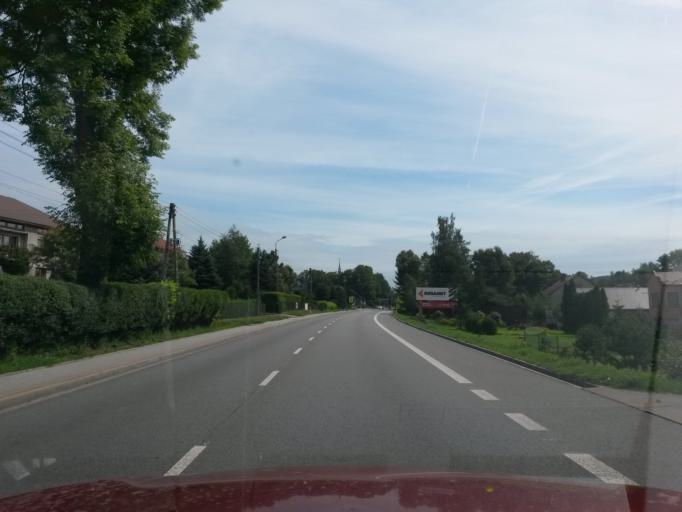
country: PL
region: Lesser Poland Voivodeship
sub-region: Powiat bochenski
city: Lapczyca
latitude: 49.9605
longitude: 20.3704
